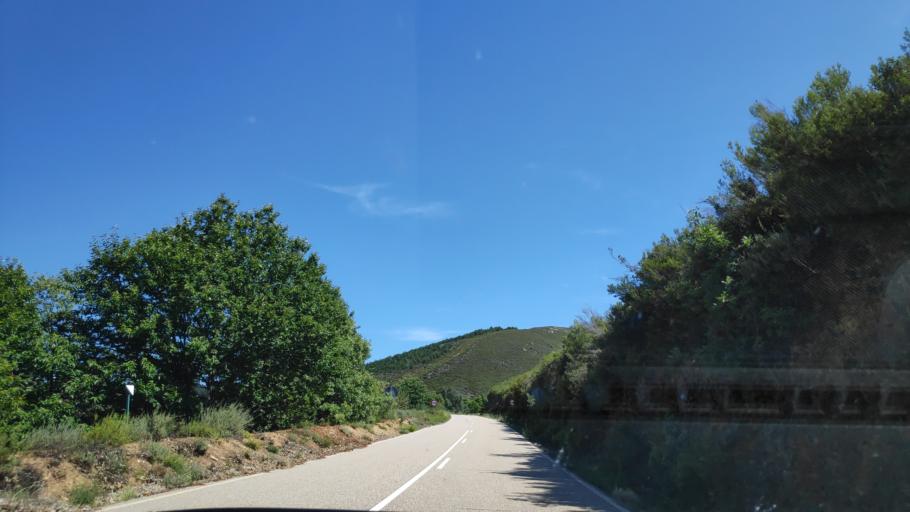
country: ES
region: Castille and Leon
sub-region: Provincia de Zamora
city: Requejo
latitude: 41.9785
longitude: -6.7137
